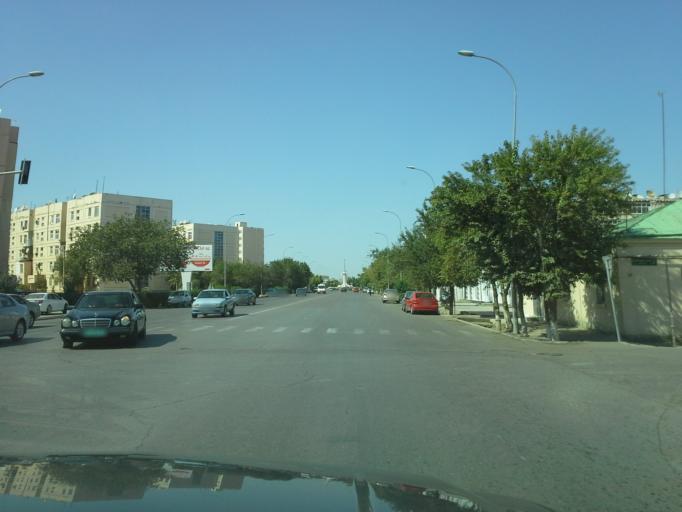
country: TM
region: Dasoguz
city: Dasoguz
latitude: 41.8297
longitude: 59.9731
